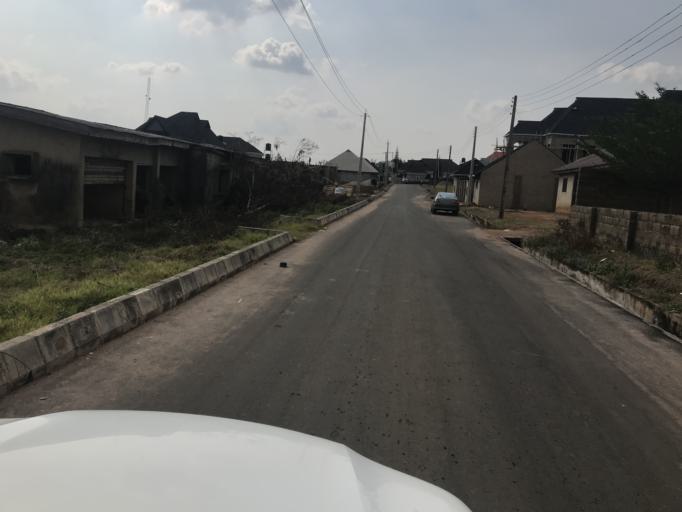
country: NG
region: Osun
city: Osogbo
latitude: 7.8109
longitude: 4.5540
